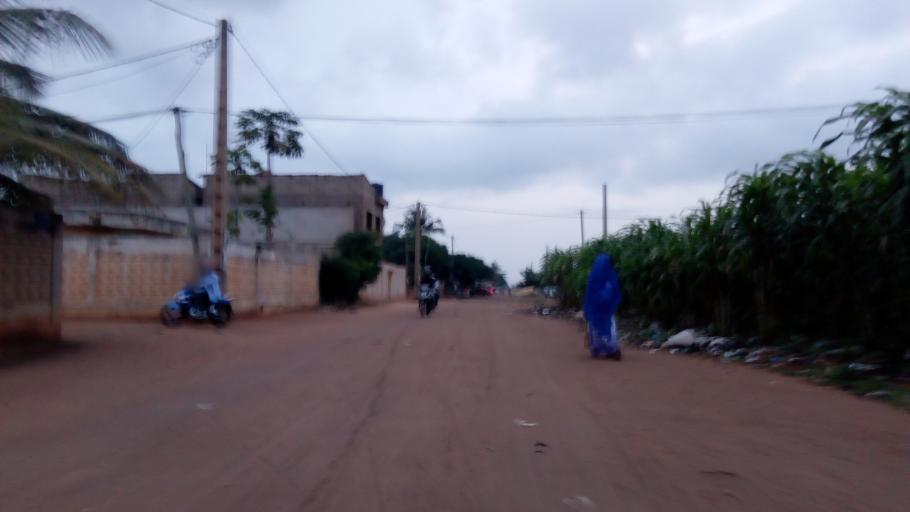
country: TG
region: Maritime
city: Lome
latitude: 6.1869
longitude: 1.1772
